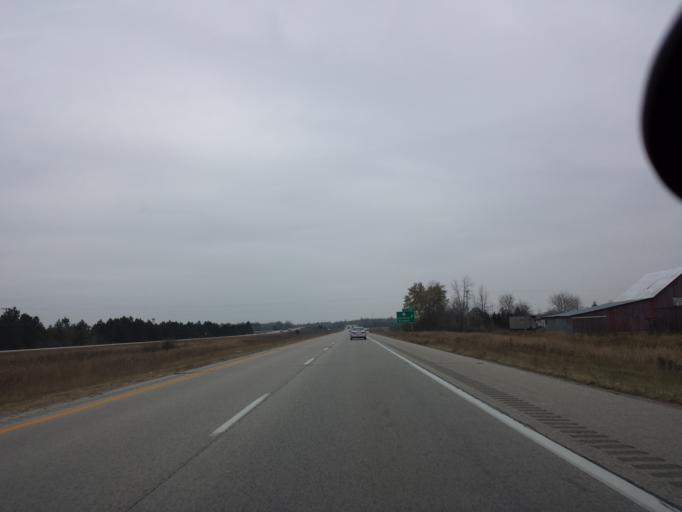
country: US
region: Michigan
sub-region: Arenac County
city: Standish
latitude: 43.9742
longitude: -84.0161
